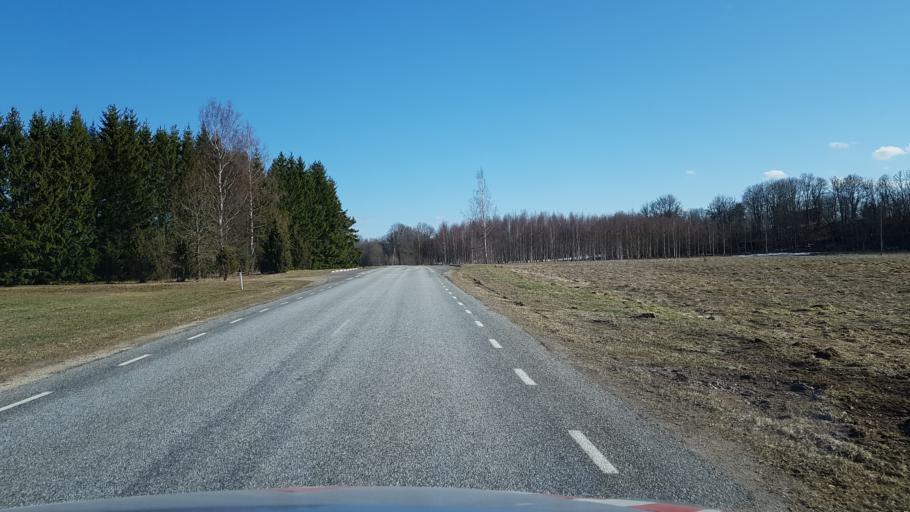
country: EE
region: Laeaene-Virumaa
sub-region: Haljala vald
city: Haljala
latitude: 59.4805
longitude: 26.1555
